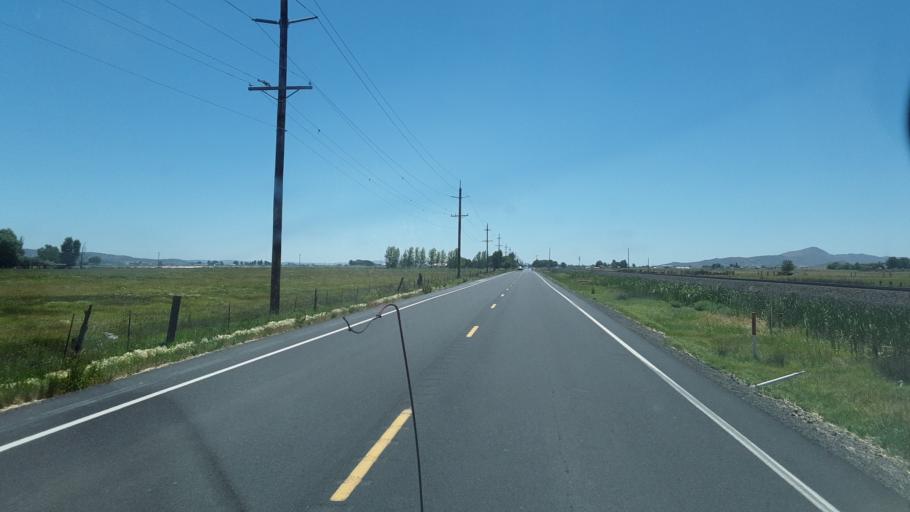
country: US
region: Oregon
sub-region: Klamath County
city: Altamont
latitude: 42.0557
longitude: -121.6450
